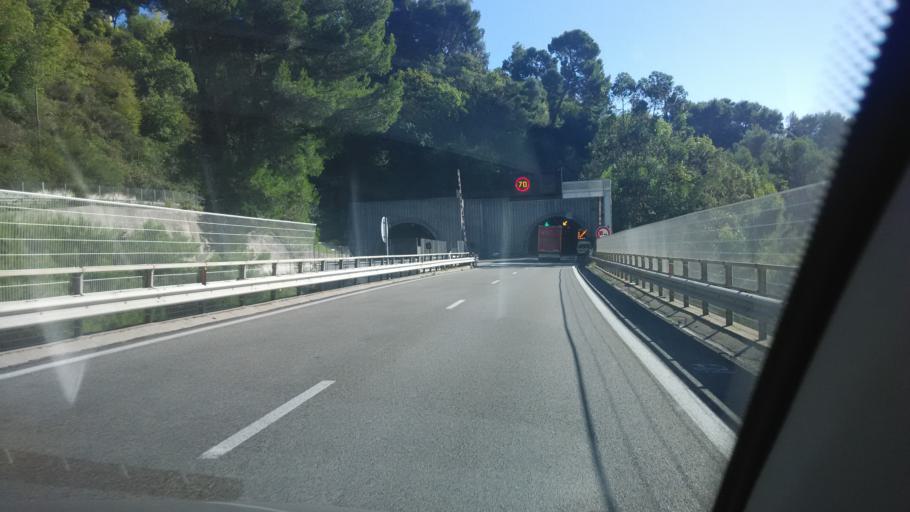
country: FR
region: Provence-Alpes-Cote d'Azur
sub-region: Departement des Alpes-Maritimes
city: Menton
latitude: 43.7961
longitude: 7.4919
